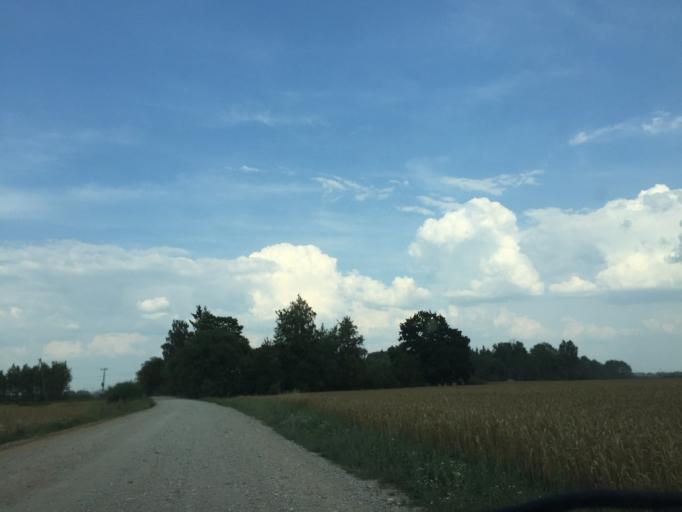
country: LT
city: Zagare
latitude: 56.4185
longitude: 23.1924
